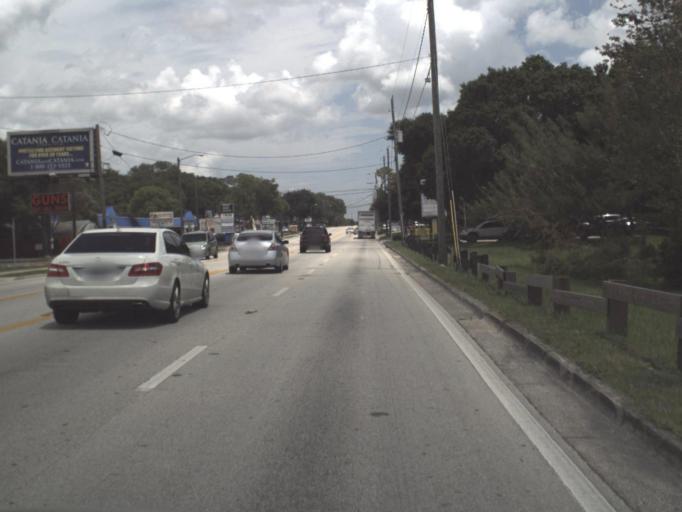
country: US
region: Florida
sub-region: Hillsborough County
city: Carrollwood
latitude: 28.0334
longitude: -82.4772
